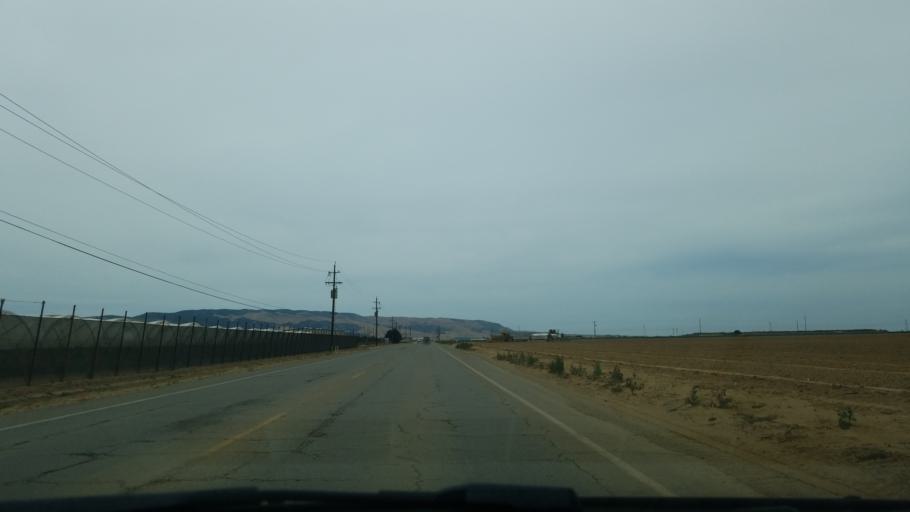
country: US
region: California
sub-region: Santa Barbara County
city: Santa Maria
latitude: 34.9211
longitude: -120.4839
